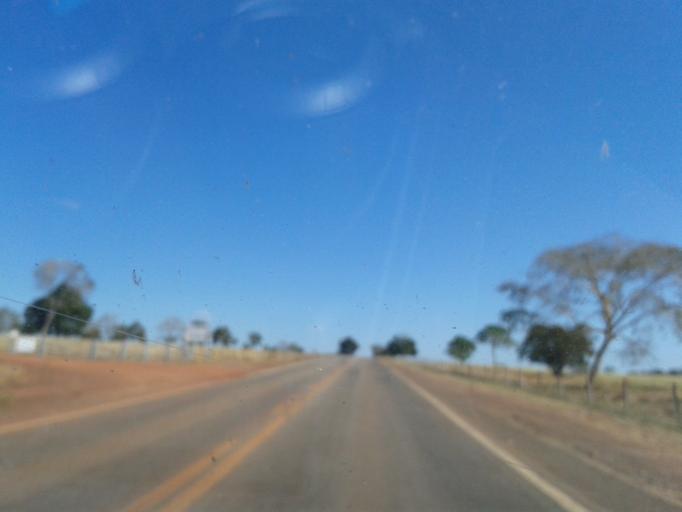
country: BR
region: Goias
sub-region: Crixas
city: Crixas
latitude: -14.1560
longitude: -50.3633
